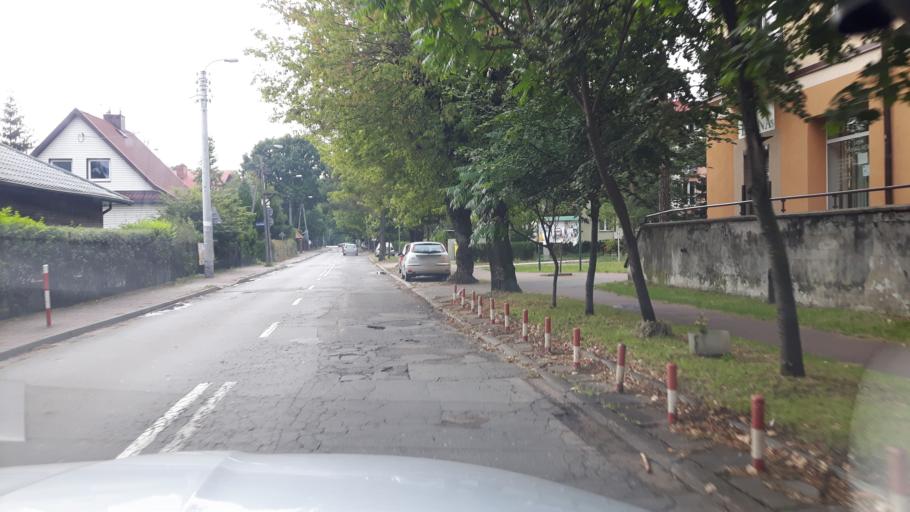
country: PL
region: Masovian Voivodeship
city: Zielonka
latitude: 52.3157
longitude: 21.1481
